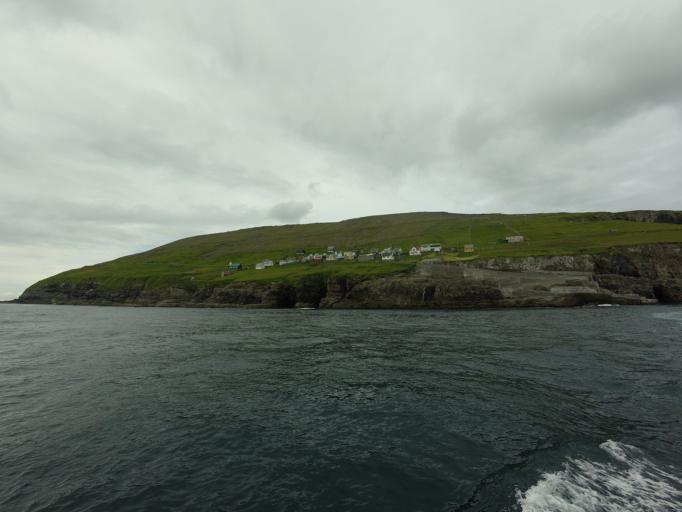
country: FO
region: Nordoyar
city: Klaksvik
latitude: 62.3156
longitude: -6.3169
